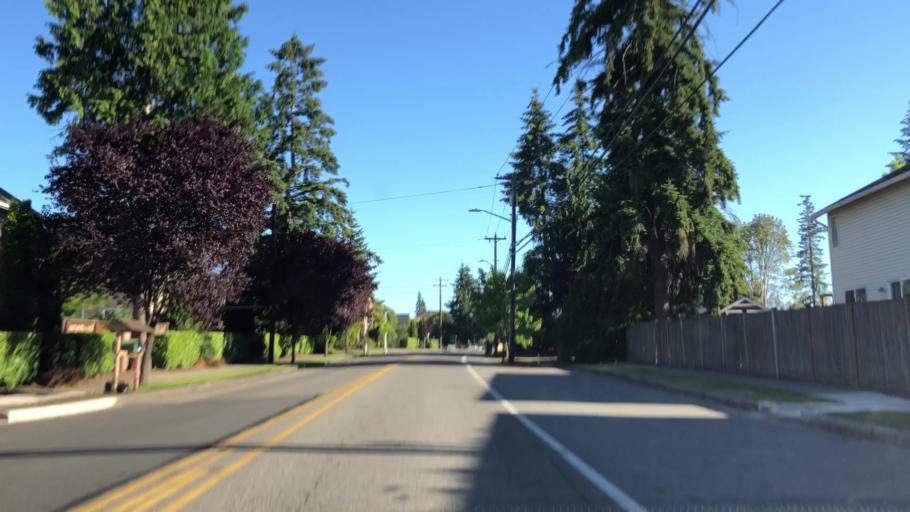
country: US
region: Washington
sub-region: Snohomish County
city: Martha Lake
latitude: 47.8143
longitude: -122.2439
